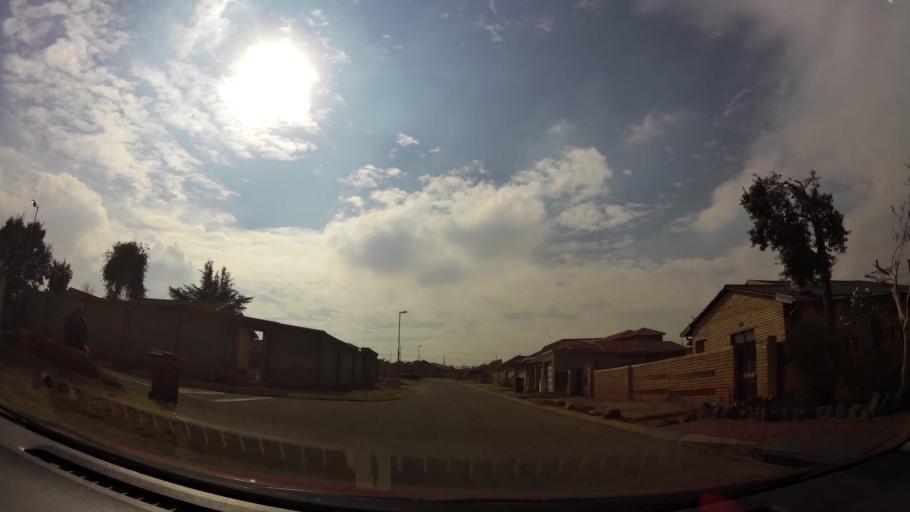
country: ZA
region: Gauteng
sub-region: City of Johannesburg Metropolitan Municipality
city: Soweto
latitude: -26.2639
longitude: 27.8272
